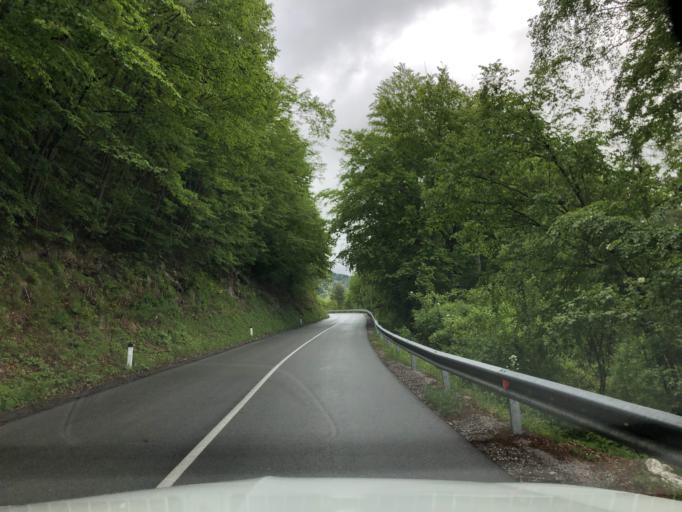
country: SI
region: Jesenice
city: Slovenski Javornik
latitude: 46.4159
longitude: 14.0884
